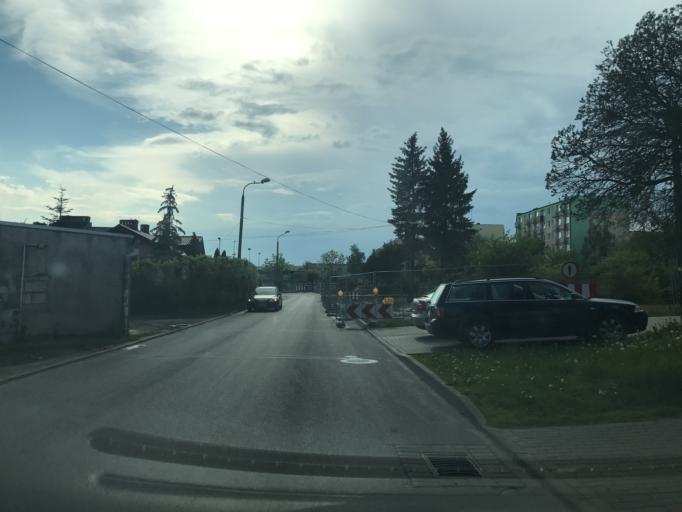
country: PL
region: Kujawsko-Pomorskie
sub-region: Powiat swiecki
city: Swiecie
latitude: 53.4087
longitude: 18.4337
